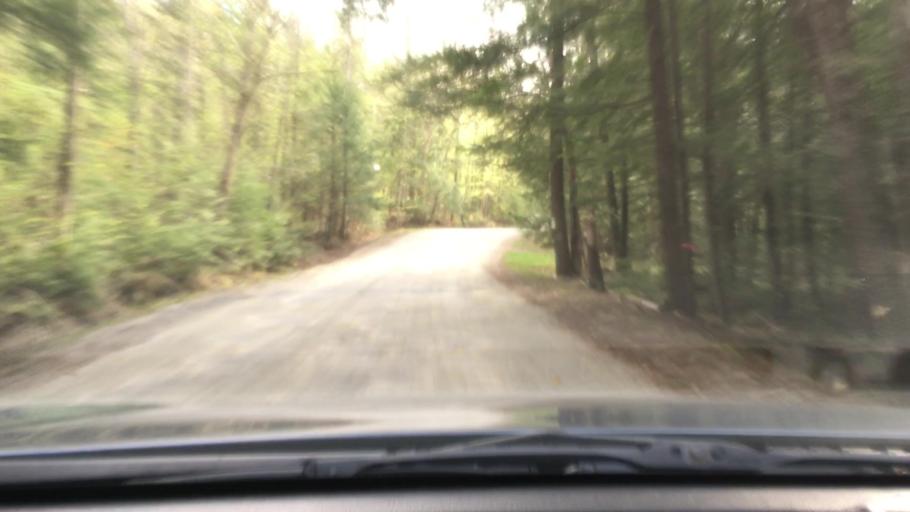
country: US
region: New York
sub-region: Warren County
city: Warrensburg
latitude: 43.8128
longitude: -73.7505
